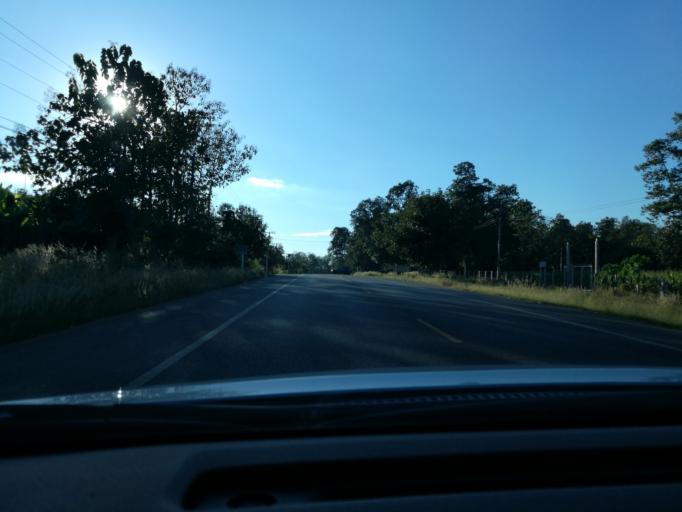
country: TH
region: Phitsanulok
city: Nakhon Thai
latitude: 17.0699
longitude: 100.8462
